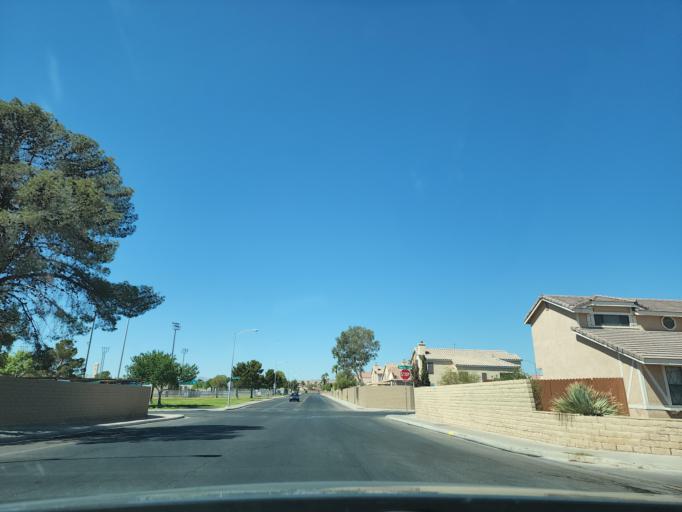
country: US
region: Nevada
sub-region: Clark County
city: Spring Valley
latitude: 36.1085
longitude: -115.2536
